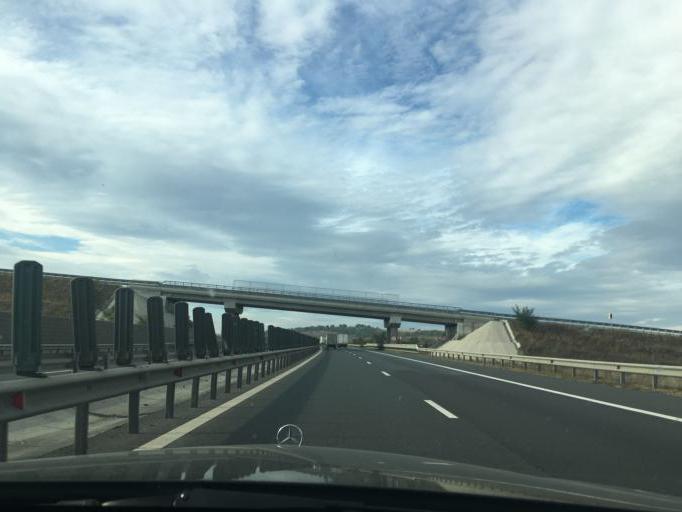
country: RO
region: Sibiu
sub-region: Comuna Orlat
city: Orlat
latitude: 45.7864
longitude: 23.9468
